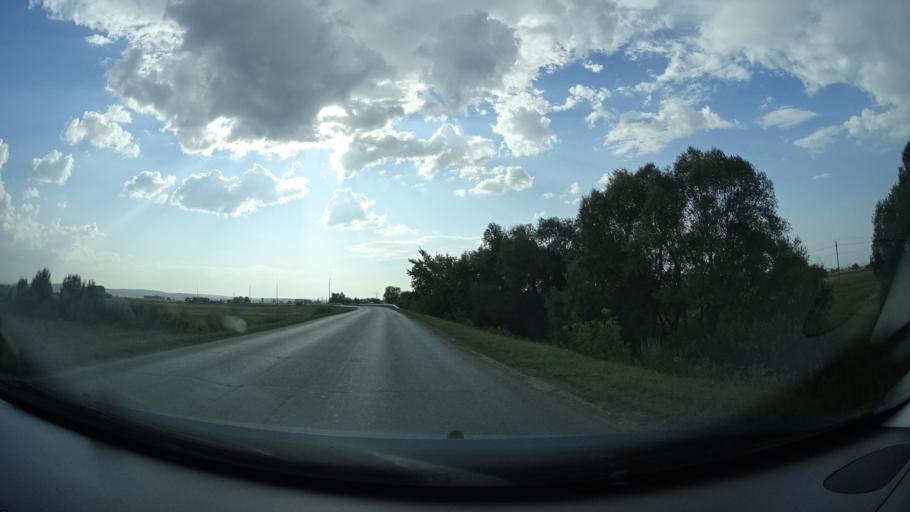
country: RU
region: Bashkortostan
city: Oktyabr'skiy
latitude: 54.4864
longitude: 53.4181
